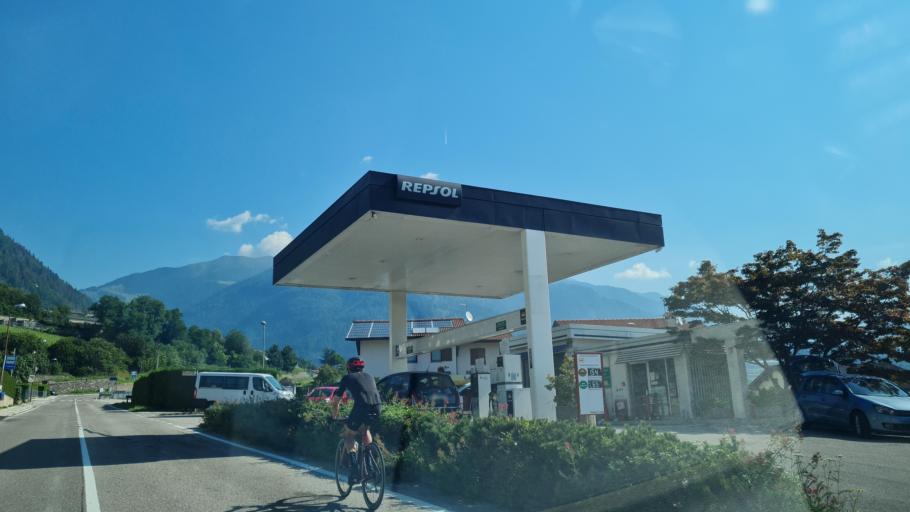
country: IT
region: Trentino-Alto Adige
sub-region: Provincia di Trento
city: Telve
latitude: 46.0691
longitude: 11.4824
